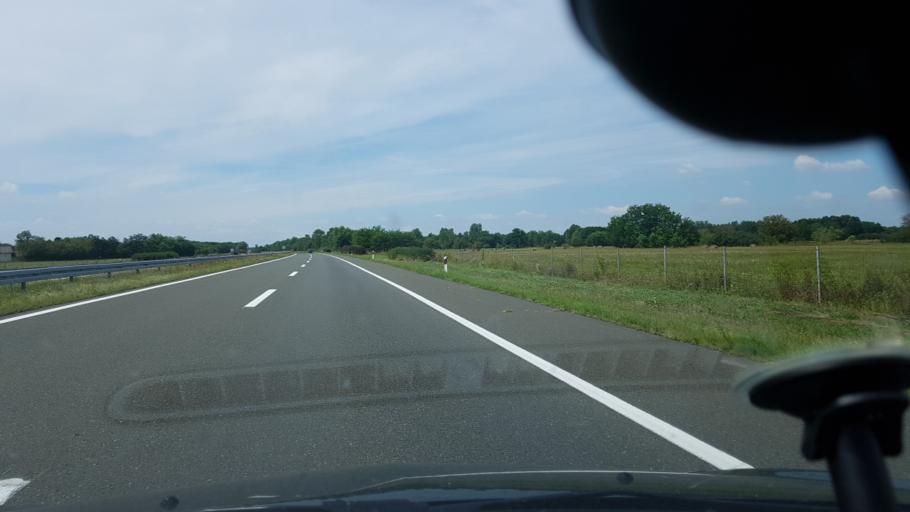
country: HR
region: Medimurska
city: Hodosan
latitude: 46.4133
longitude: 16.6255
